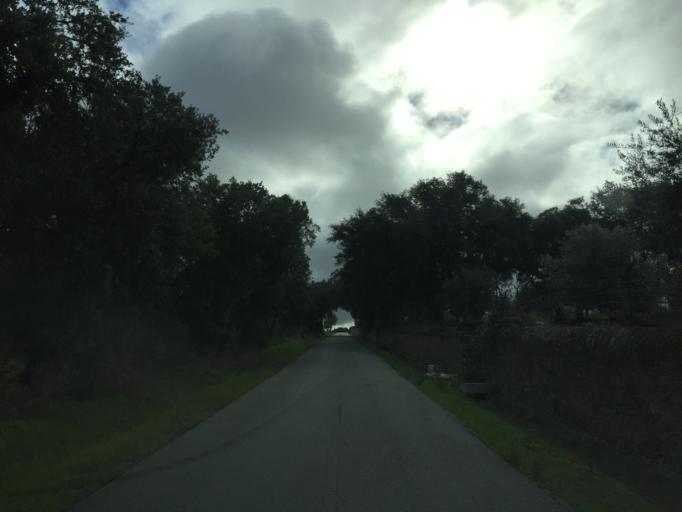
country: PT
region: Portalegre
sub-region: Alter do Chao
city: Alter do Chao
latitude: 39.2275
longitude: -7.6803
